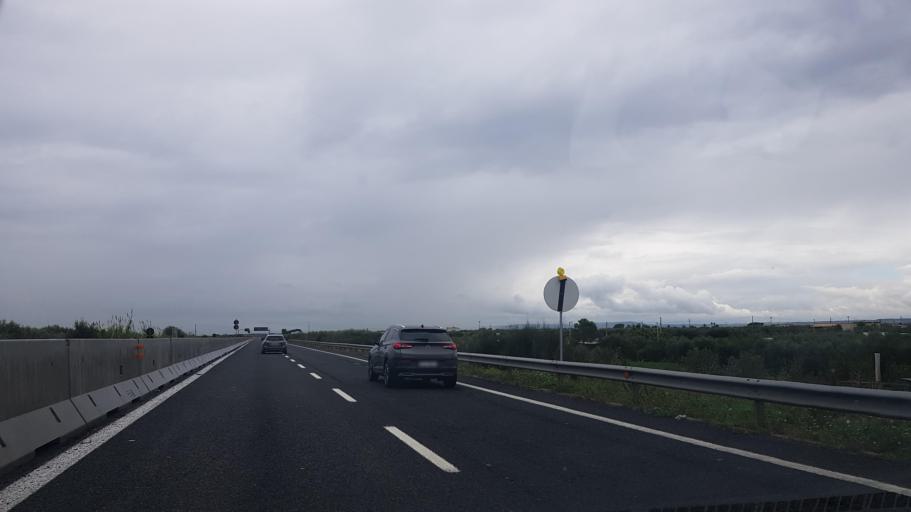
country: IT
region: Apulia
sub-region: Provincia di Taranto
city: Massafra
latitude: 40.5311
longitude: 17.1019
